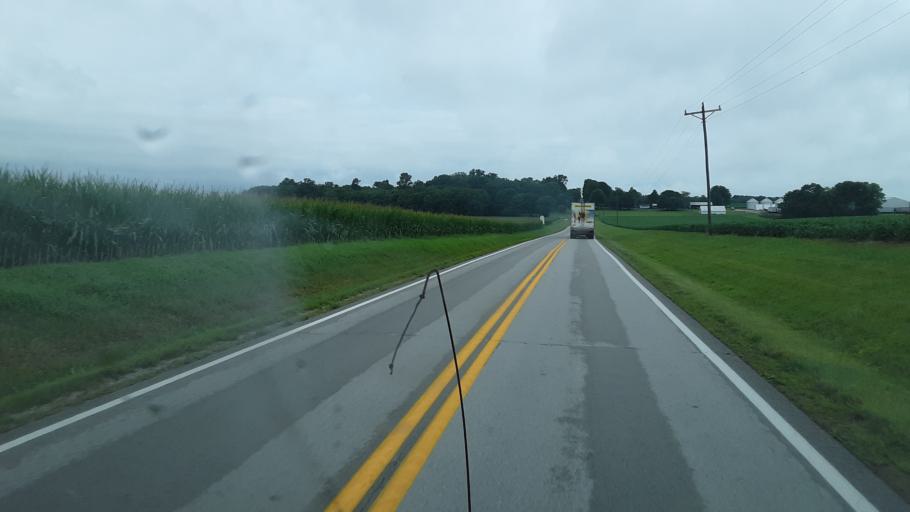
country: US
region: Kentucky
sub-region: Todd County
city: Elkton
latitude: 36.7427
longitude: -87.0568
